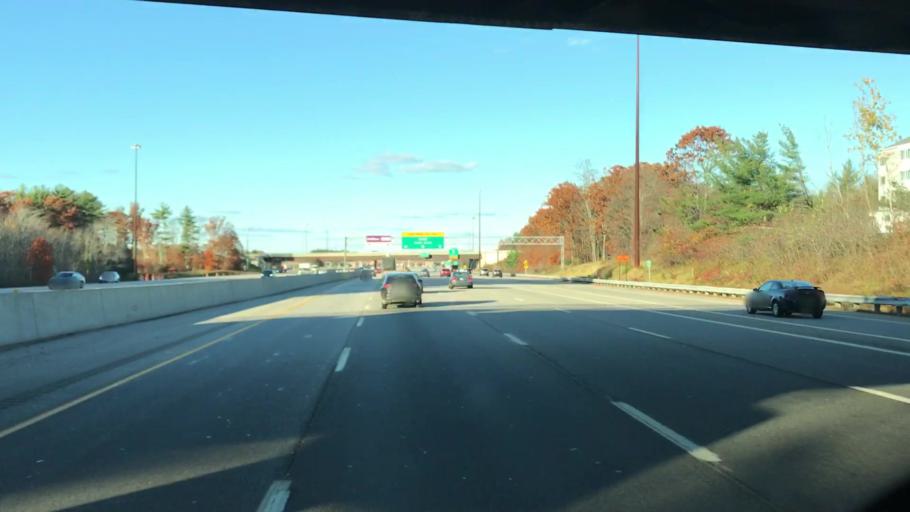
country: US
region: New Hampshire
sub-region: Rockingham County
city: Hampton
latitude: 42.9561
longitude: -70.8575
